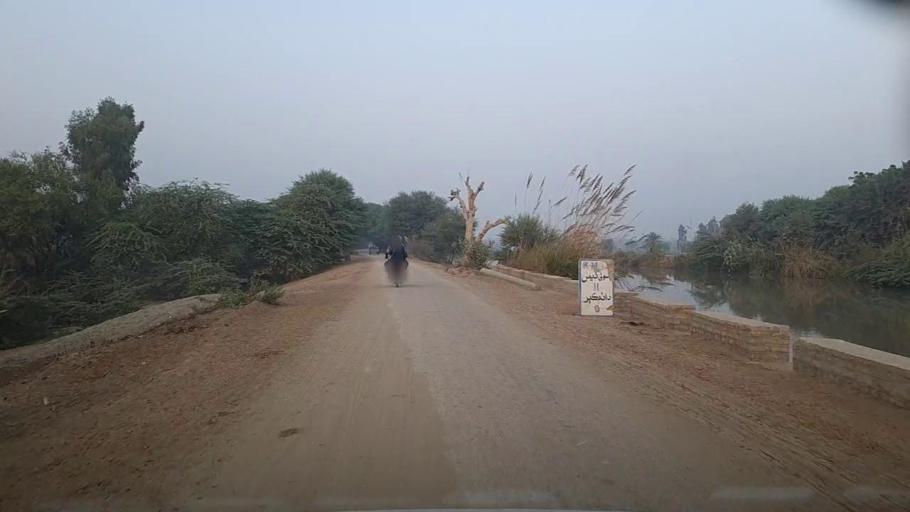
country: PK
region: Sindh
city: Bozdar
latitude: 27.0503
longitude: 68.5963
